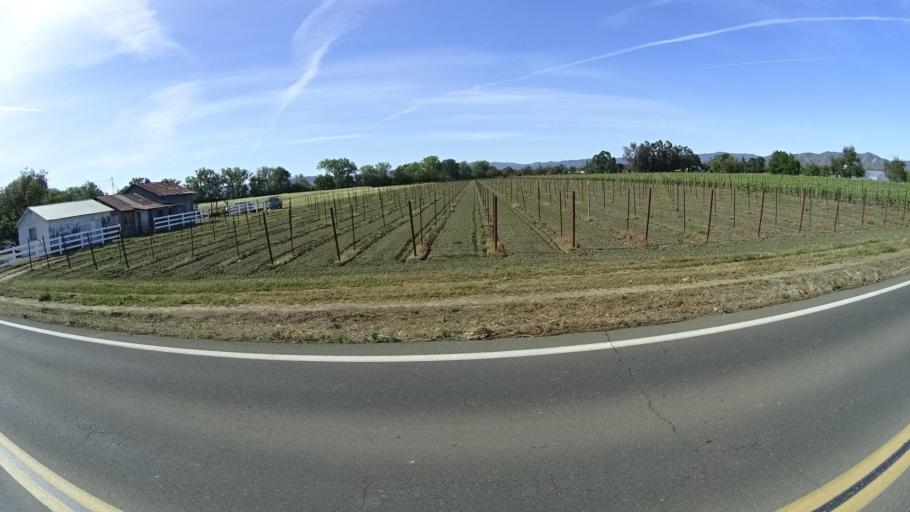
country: US
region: California
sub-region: Lake County
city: Kelseyville
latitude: 39.0151
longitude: -122.8721
